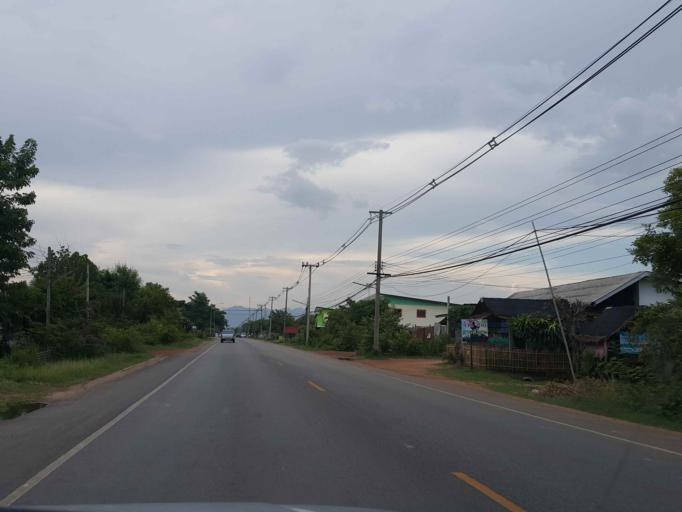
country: TH
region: Lampang
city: Hang Chat
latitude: 18.2707
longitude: 99.3868
